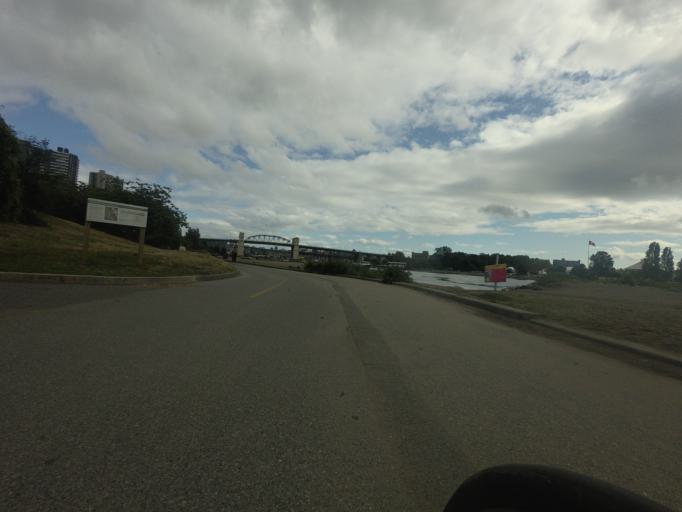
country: CA
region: British Columbia
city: West End
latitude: 49.2800
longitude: -123.1394
